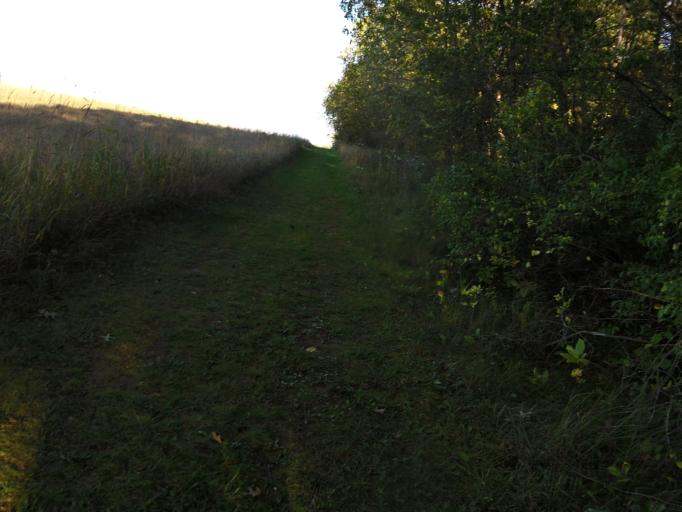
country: US
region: Minnesota
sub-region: Washington County
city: Lake Saint Croix Beach
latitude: 44.9344
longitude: -92.7962
